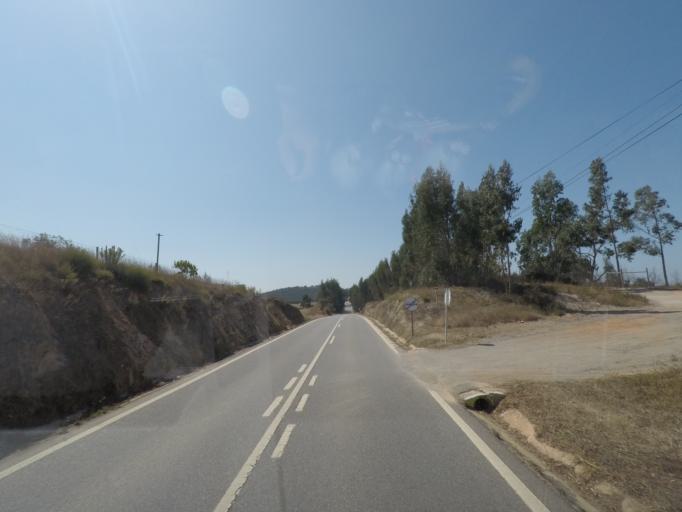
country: PT
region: Beja
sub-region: Odemira
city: Sao Teotonio
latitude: 37.5410
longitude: -8.6891
